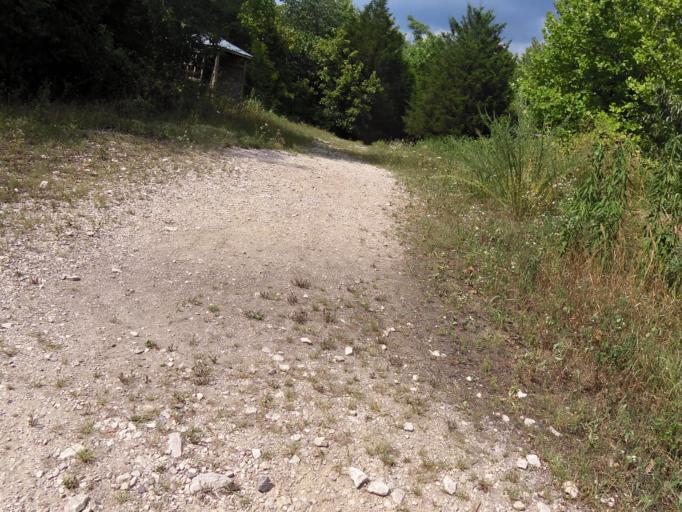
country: US
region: Tennessee
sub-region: Knox County
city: Knoxville
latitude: 35.9506
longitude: -83.8679
